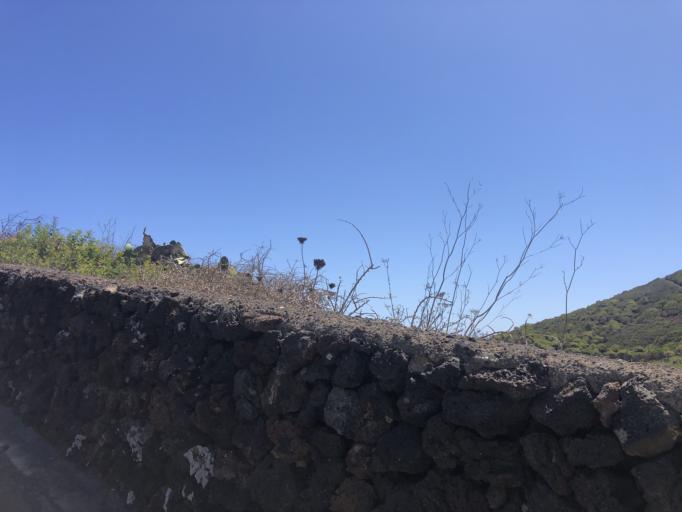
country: IT
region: Sicily
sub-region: Agrigento
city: Lampedusa
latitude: 35.8643
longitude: 12.8720
